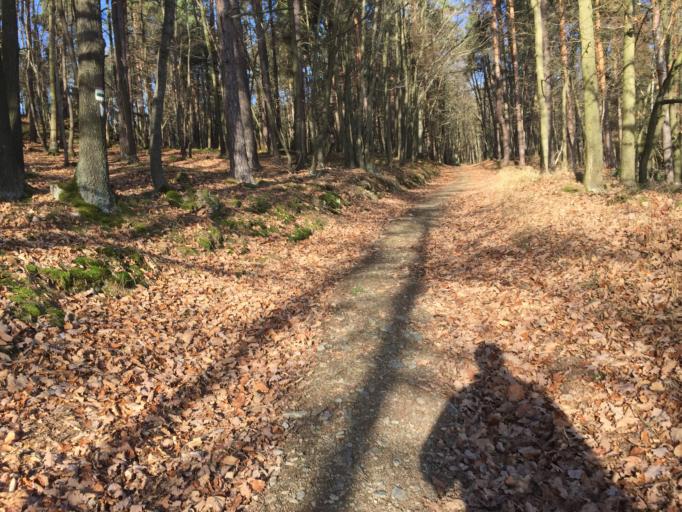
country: DE
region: Thuringia
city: Bad Blankenburg
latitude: 50.6590
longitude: 11.2723
